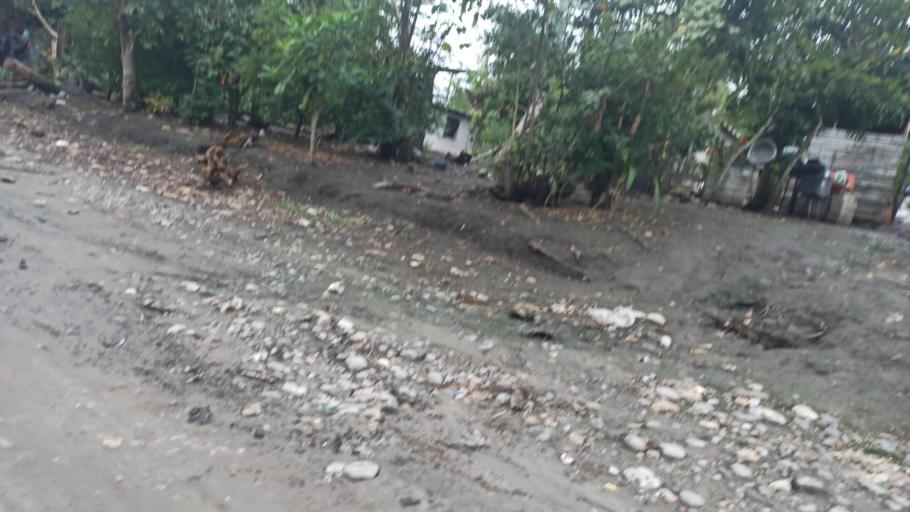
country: MX
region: Puebla
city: Espinal
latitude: 20.2884
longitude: -97.3923
